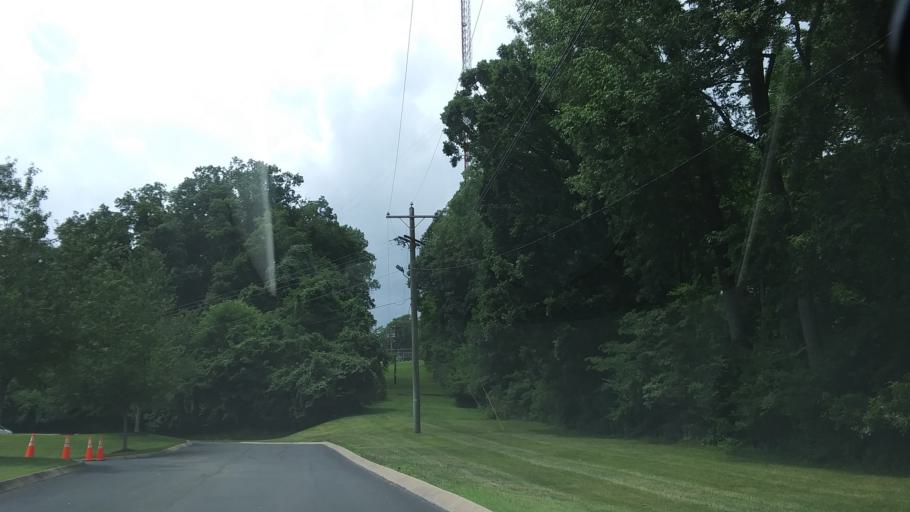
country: US
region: Tennessee
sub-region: Davidson County
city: Belle Meade
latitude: 36.1389
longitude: -86.8642
